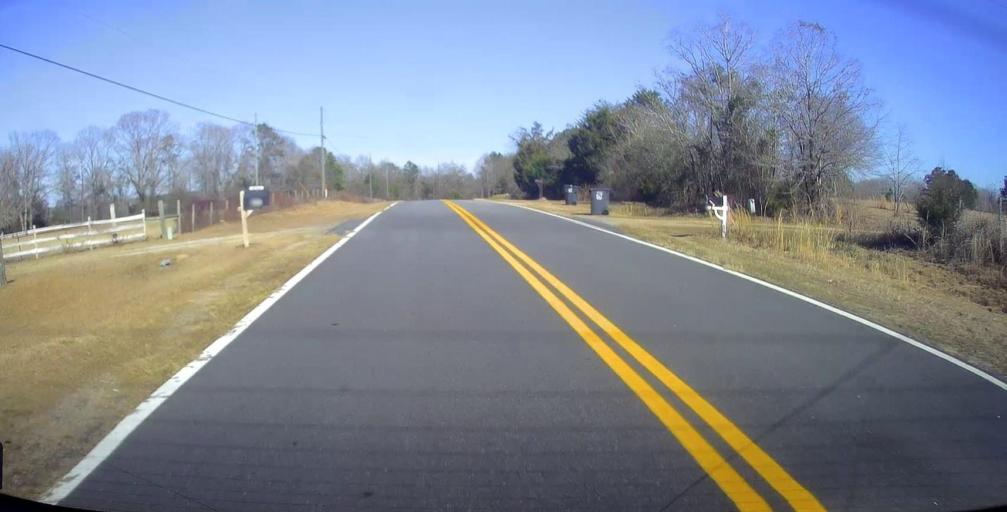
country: US
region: Georgia
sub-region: Peach County
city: Fort Valley
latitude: 32.6433
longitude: -83.9061
